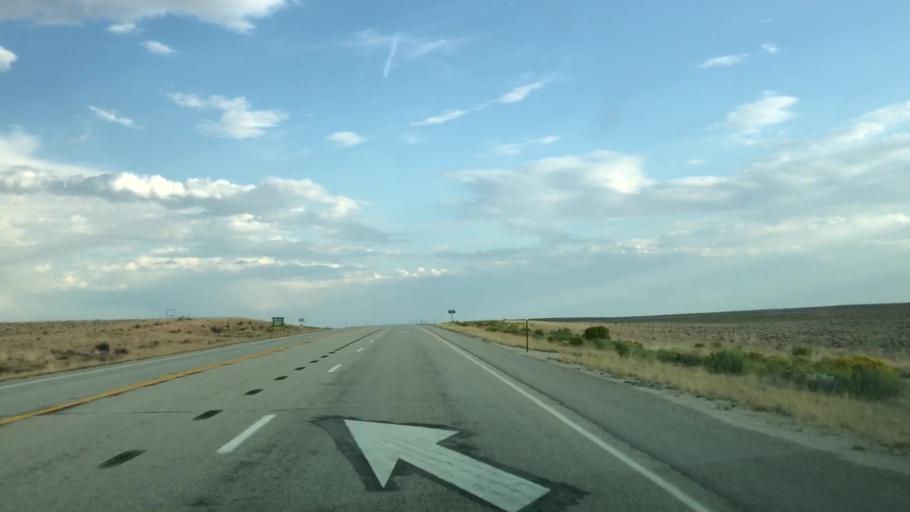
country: US
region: Wyoming
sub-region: Sweetwater County
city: North Rock Springs
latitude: 42.2647
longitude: -109.4749
